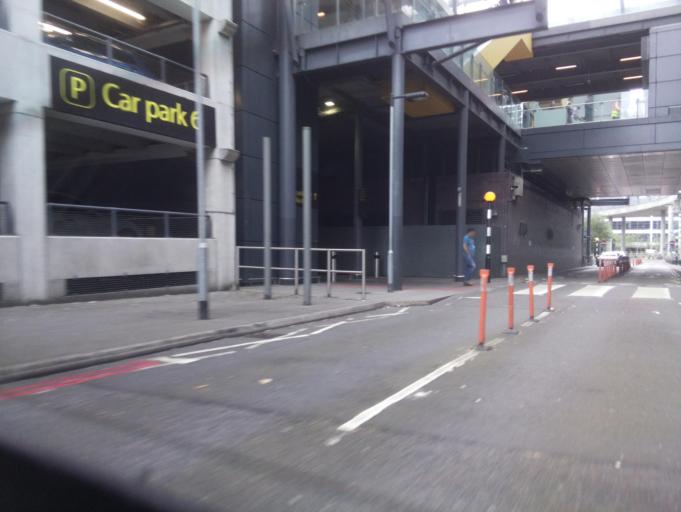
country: GB
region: England
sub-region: Surrey
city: Horley
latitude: 51.1613
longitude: -0.1766
